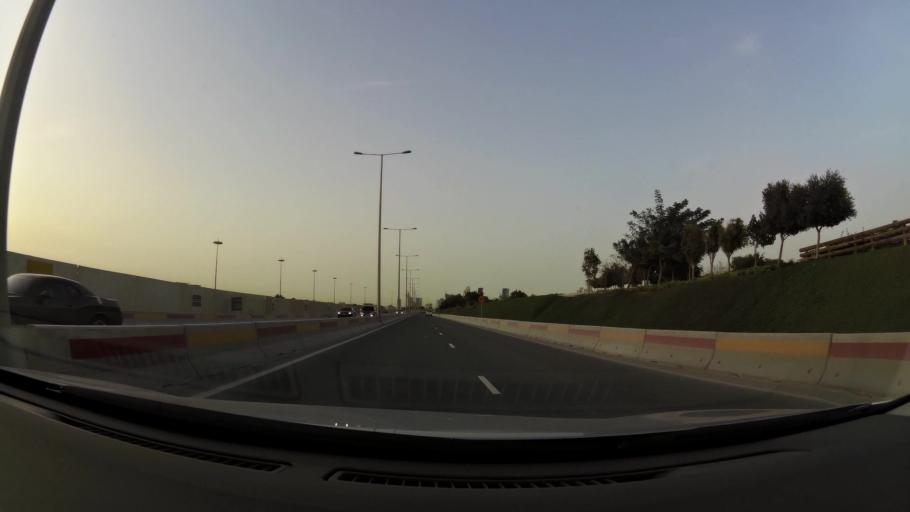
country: QA
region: Baladiyat ad Dawhah
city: Doha
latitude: 25.3540
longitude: 51.5208
